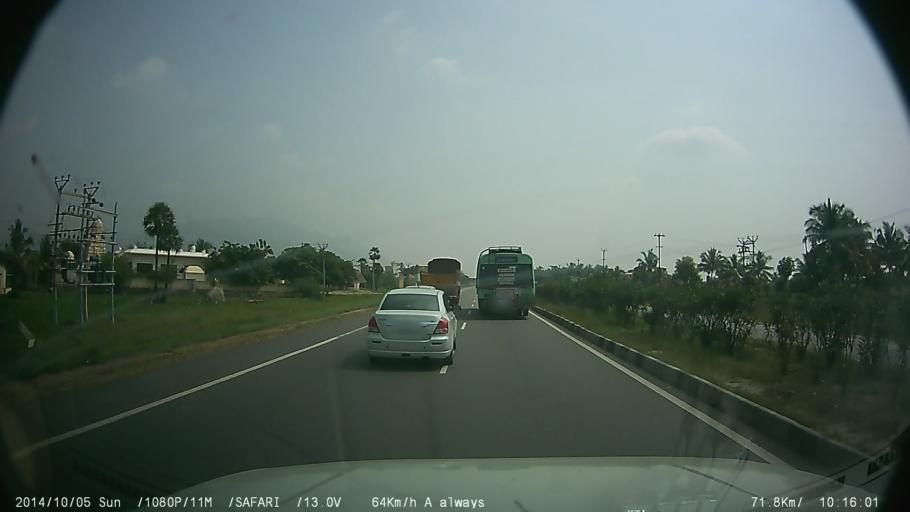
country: IN
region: Tamil Nadu
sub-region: Salem
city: Attayyampatti
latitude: 11.5642
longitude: 78.0258
